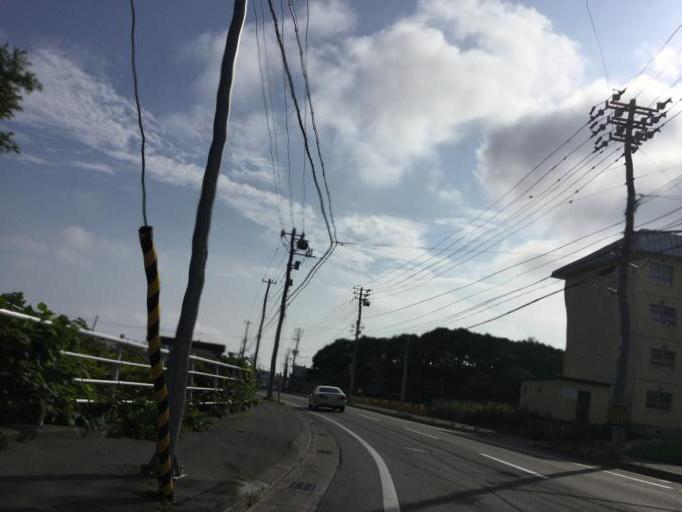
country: JP
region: Hokkaido
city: Wakkanai
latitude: 45.3937
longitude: 141.6841
